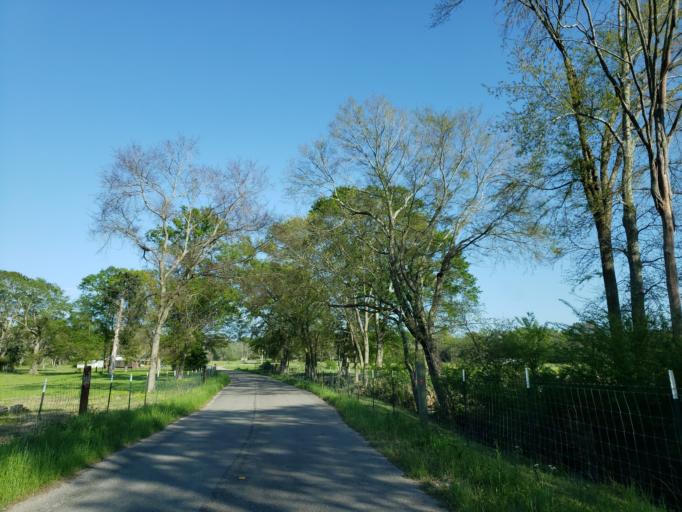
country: US
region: Mississippi
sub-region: Jones County
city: Ellisville
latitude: 31.6772
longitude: -89.3065
